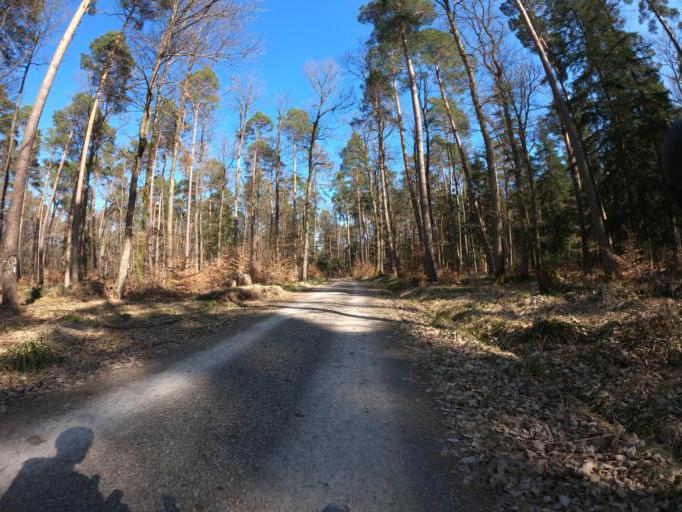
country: DE
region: Baden-Wuerttemberg
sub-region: Tuebingen Region
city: Rangendingen
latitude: 48.3942
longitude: 8.9209
